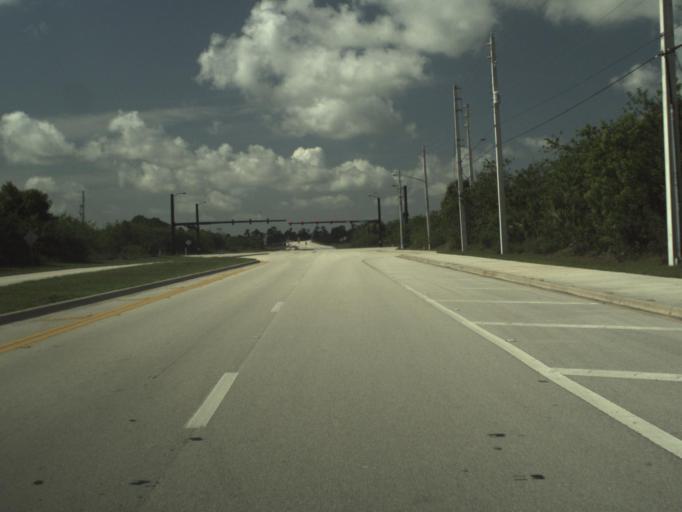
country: US
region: Florida
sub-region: Saint Lucie County
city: Port Saint Lucie
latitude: 27.2115
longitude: -80.3721
